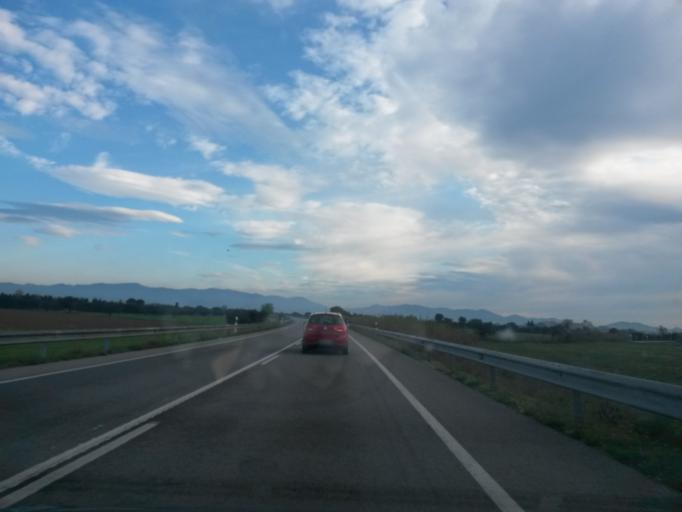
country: ES
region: Catalonia
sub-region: Provincia de Girona
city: Vilamalla
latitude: 42.2396
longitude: 2.9833
